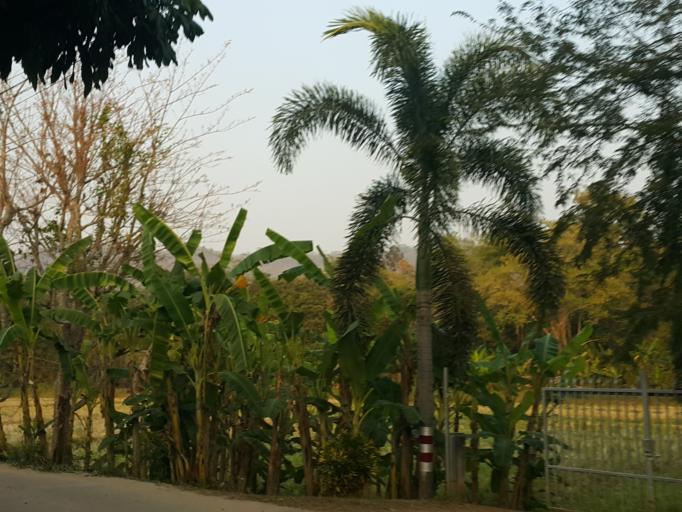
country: TH
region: Chiang Mai
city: Mae Taeng
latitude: 19.1099
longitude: 98.8283
